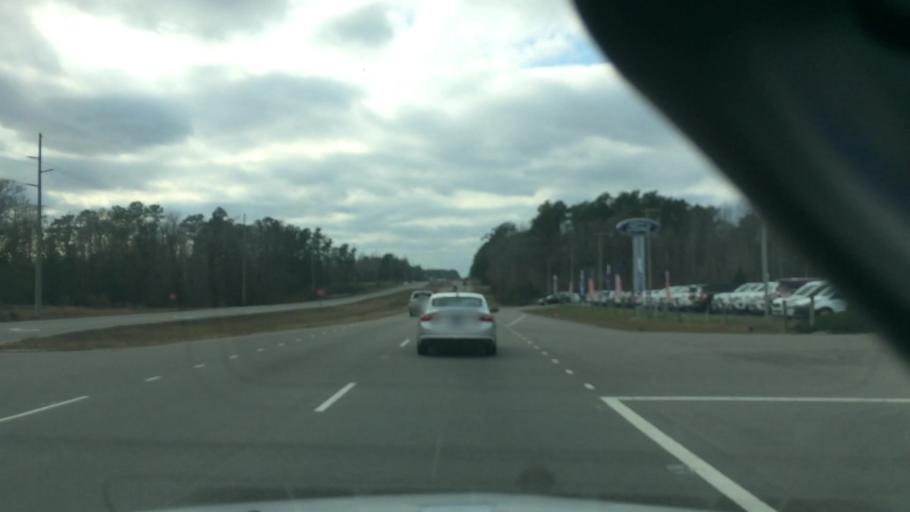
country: US
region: North Carolina
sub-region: Brunswick County
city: Shallotte
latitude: 33.9917
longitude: -78.3469
